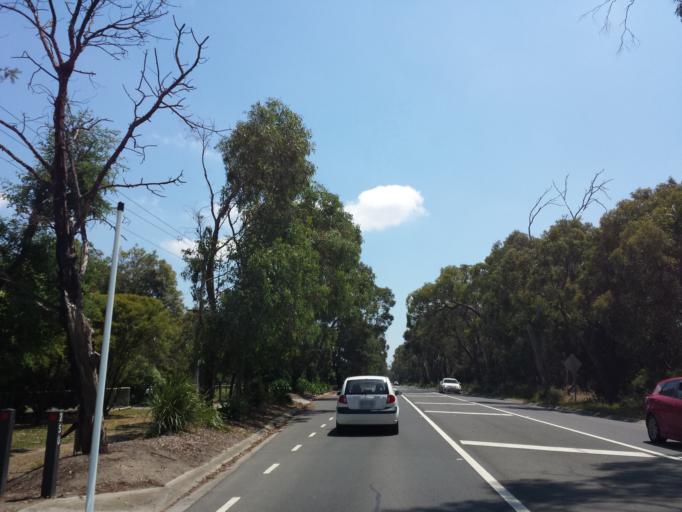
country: AU
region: Victoria
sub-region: Maroondah
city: Kilsyth South
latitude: -37.8259
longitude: 145.3178
